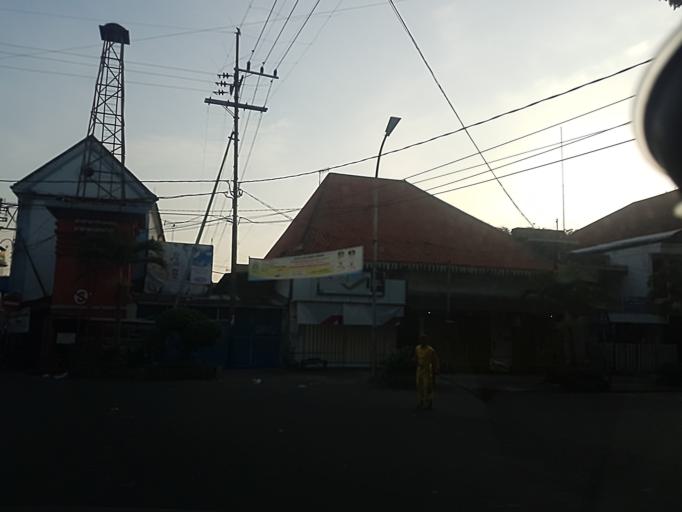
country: ID
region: East Java
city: Gresik
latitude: -7.1546
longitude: 112.6563
